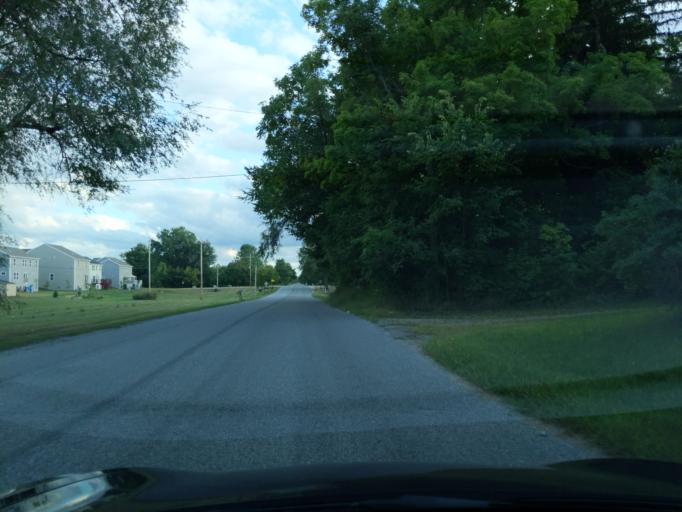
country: US
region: Michigan
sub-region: Ingham County
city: Holt
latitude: 42.6327
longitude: -84.5824
